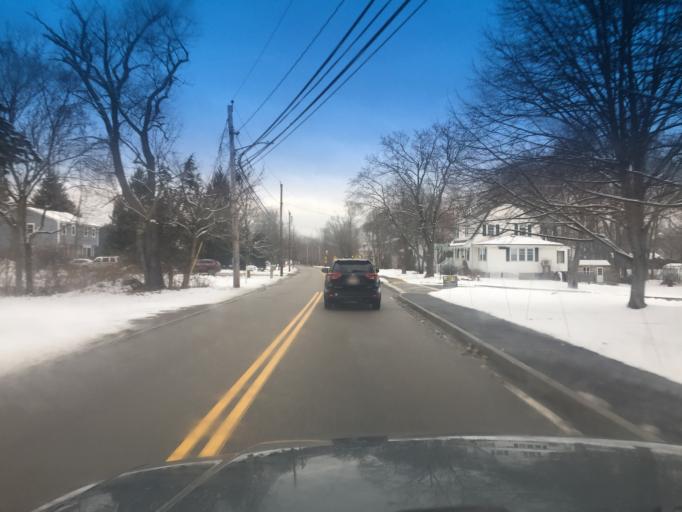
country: US
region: Massachusetts
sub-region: Norfolk County
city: Millis
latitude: 42.1782
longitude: -71.3611
